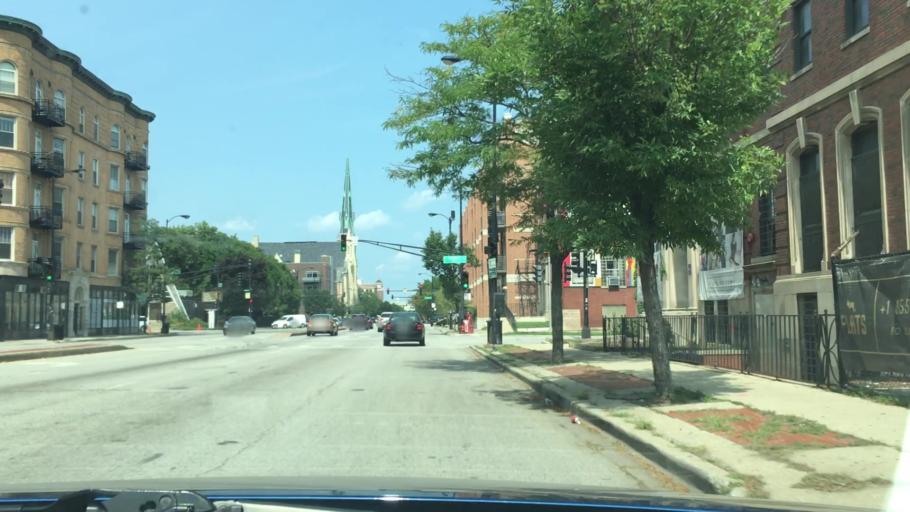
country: US
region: Illinois
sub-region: Cook County
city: Chicago
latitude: 41.8798
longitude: -87.6667
